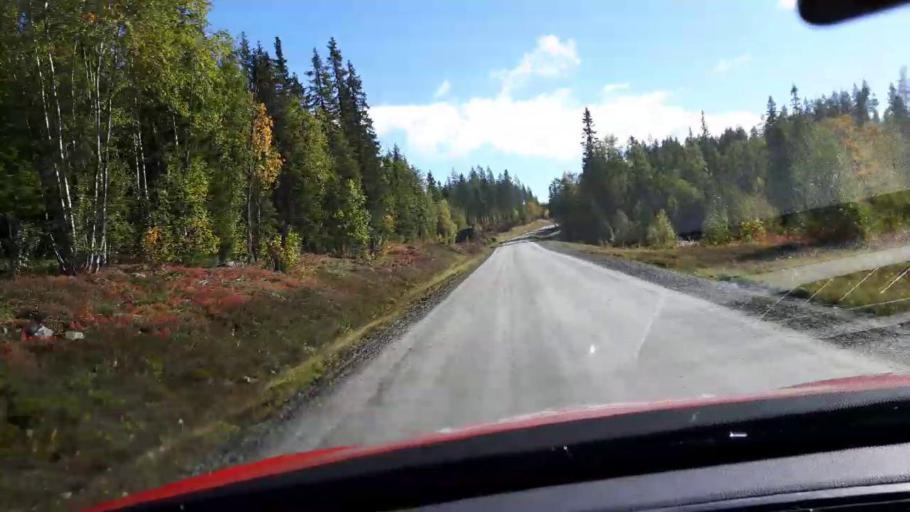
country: NO
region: Nord-Trondelag
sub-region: Lierne
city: Sandvika
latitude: 64.6118
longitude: 13.9502
